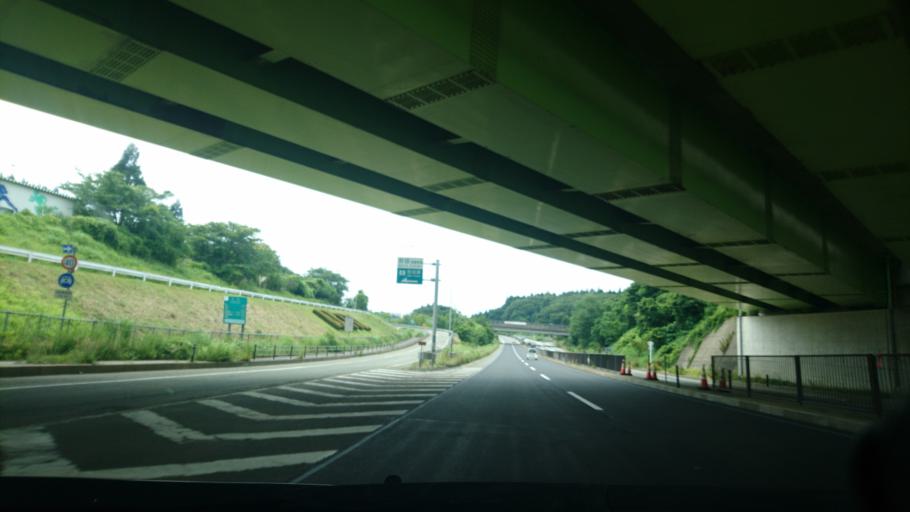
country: JP
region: Akita
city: Akita
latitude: 39.6615
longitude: 140.1901
